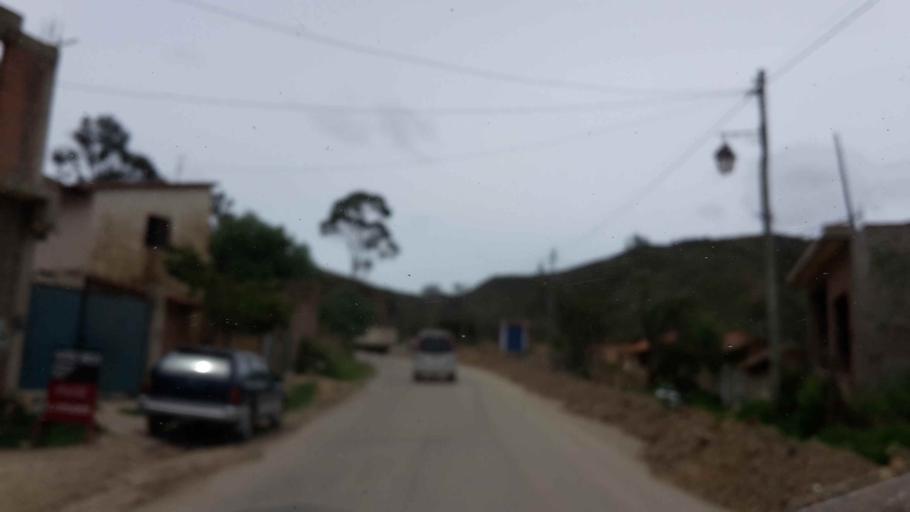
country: BO
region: Cochabamba
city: Totora
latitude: -17.7312
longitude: -65.1905
